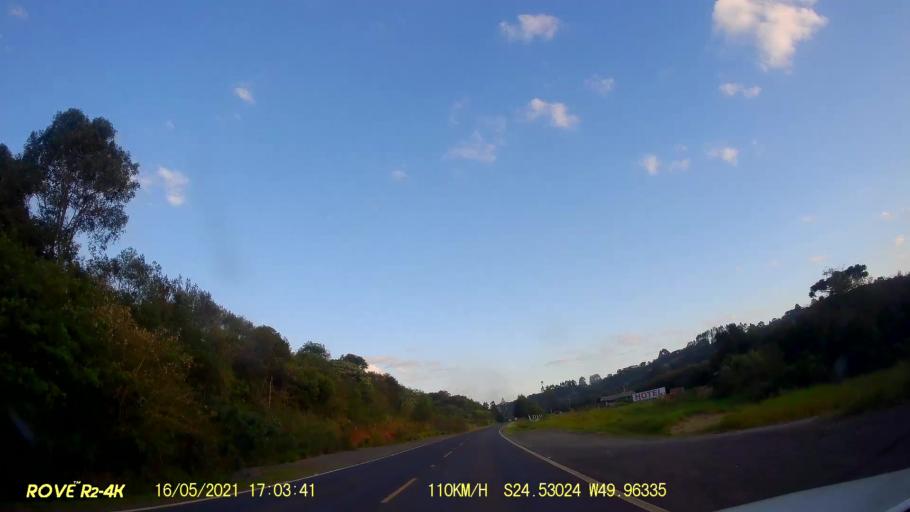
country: BR
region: Parana
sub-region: Pirai Do Sul
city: Pirai do Sul
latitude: -24.5301
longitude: -49.9634
